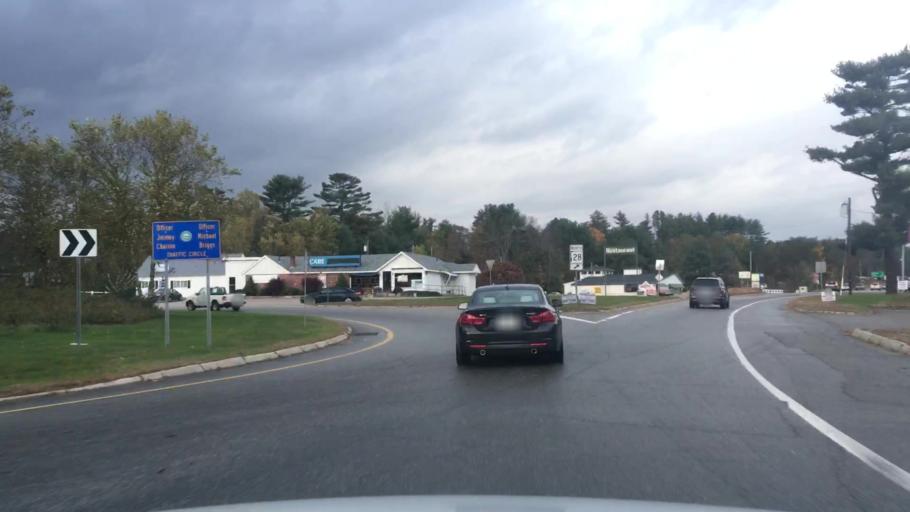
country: US
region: New Hampshire
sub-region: Merrimack County
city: Epsom
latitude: 43.2279
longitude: -71.3600
